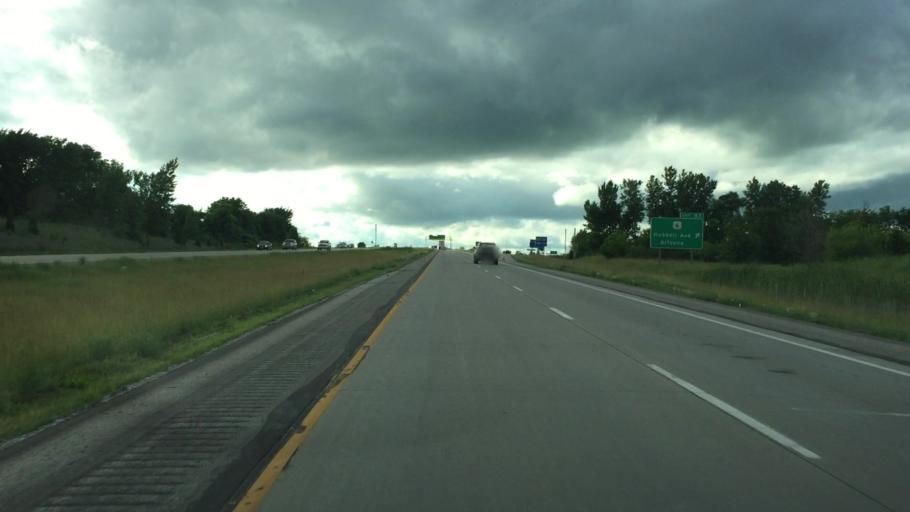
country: US
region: Iowa
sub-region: Polk County
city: Altoona
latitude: 41.6386
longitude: -93.5066
